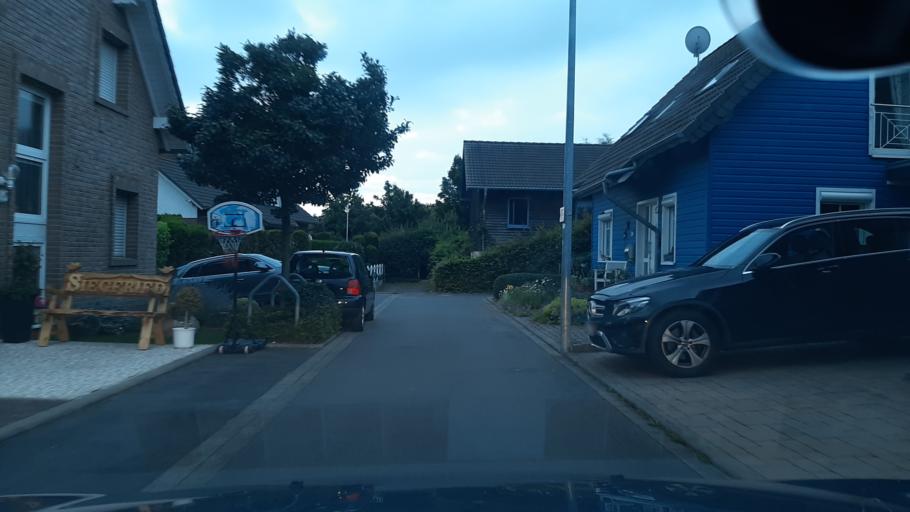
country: DE
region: North Rhine-Westphalia
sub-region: Regierungsbezirk Koln
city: Mechernich
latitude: 50.5966
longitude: 6.6609
